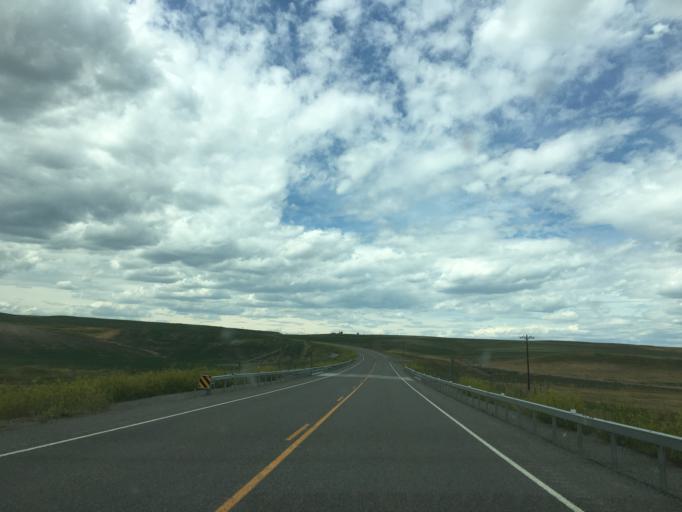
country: US
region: Montana
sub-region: Teton County
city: Choteau
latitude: 48.1345
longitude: -112.3897
